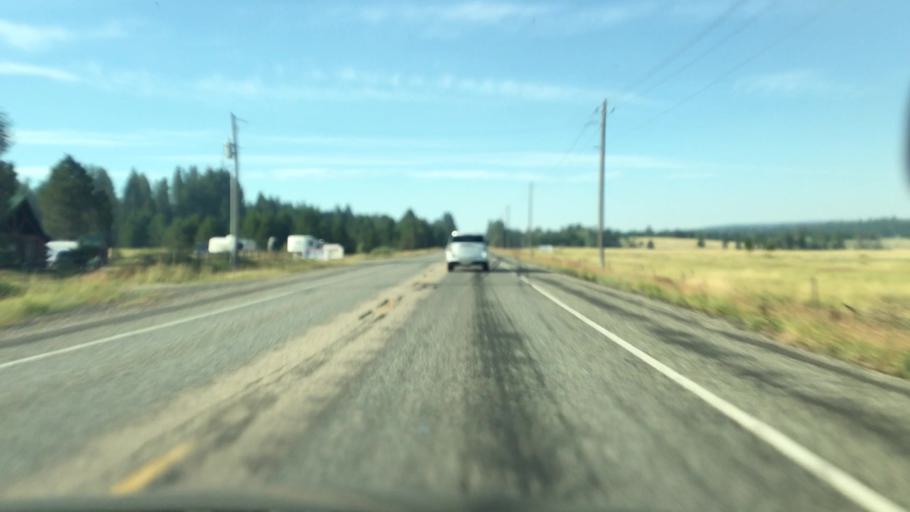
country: US
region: Idaho
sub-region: Valley County
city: Cascade
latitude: 44.3574
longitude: -116.0223
